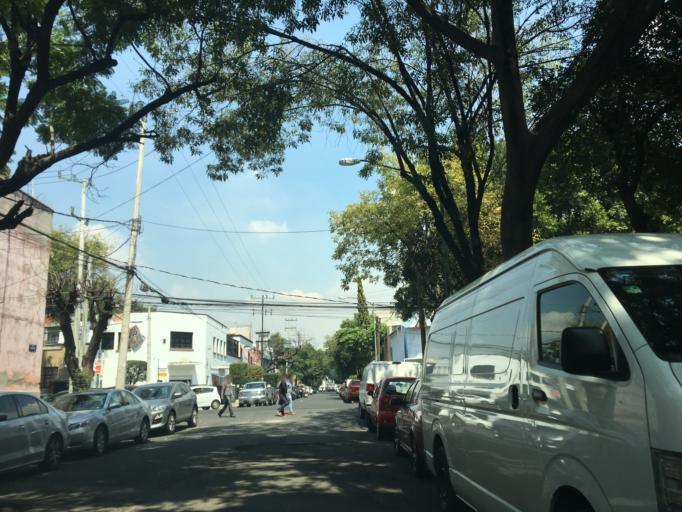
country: MX
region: Mexico City
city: Benito Juarez
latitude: 19.4048
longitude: -99.1408
